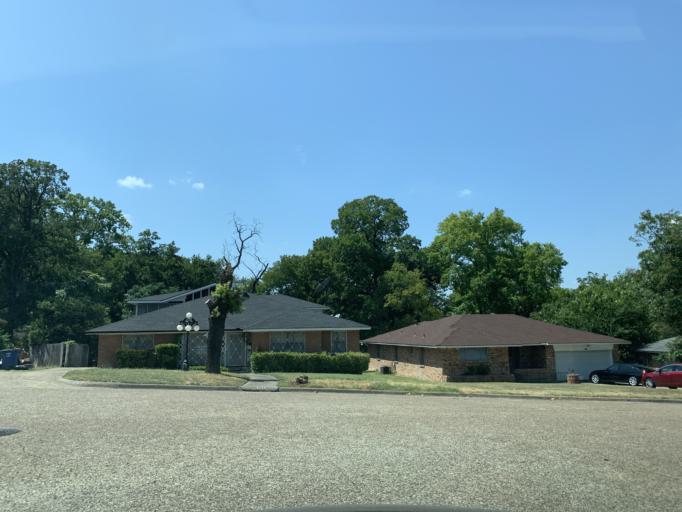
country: US
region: Texas
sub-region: Dallas County
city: Cockrell Hill
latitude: 32.6822
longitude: -96.8088
